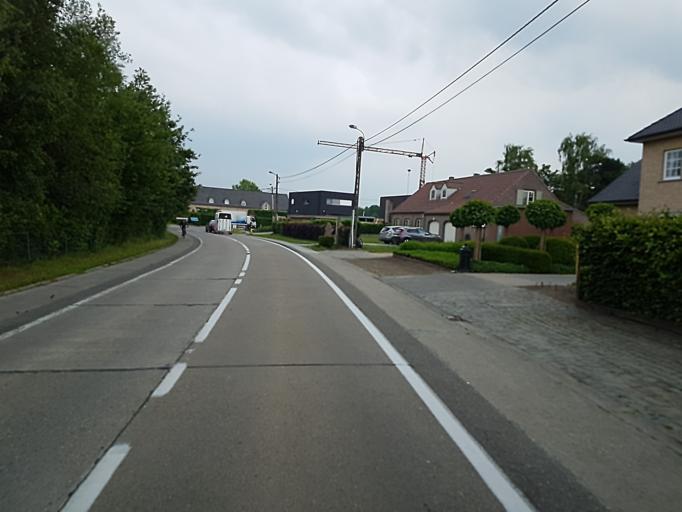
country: BE
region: Flanders
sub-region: Provincie Antwerpen
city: Putte
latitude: 51.0704
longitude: 4.6568
